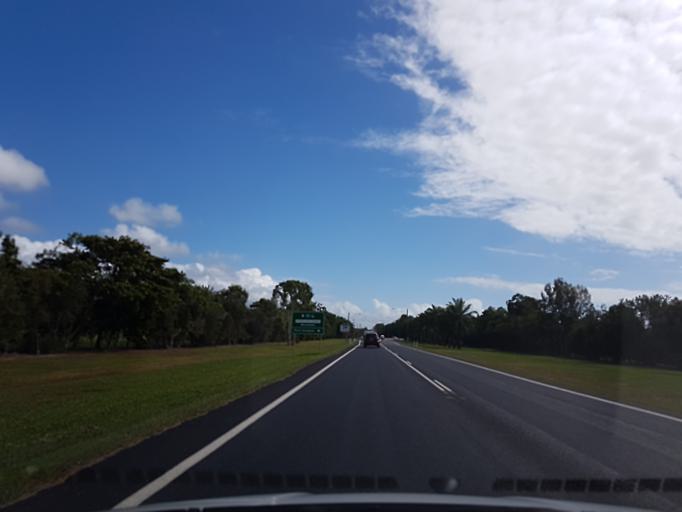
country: AU
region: Queensland
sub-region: Cairns
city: Port Douglas
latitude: -16.5311
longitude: 145.4640
